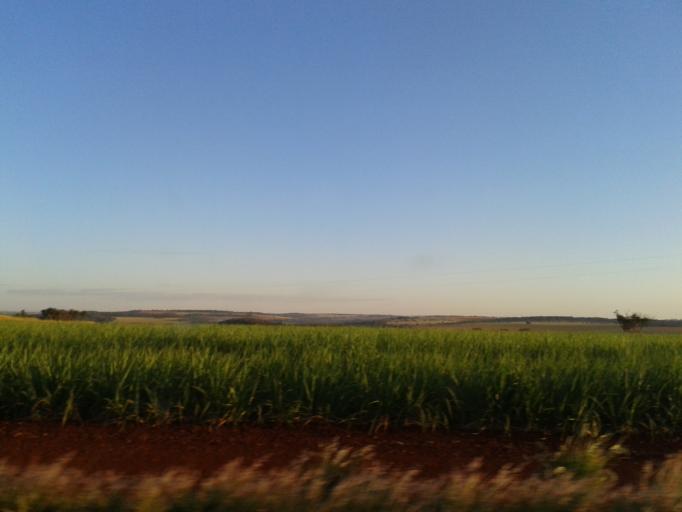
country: BR
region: Minas Gerais
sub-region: Centralina
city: Centralina
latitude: -18.6982
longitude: -49.3197
